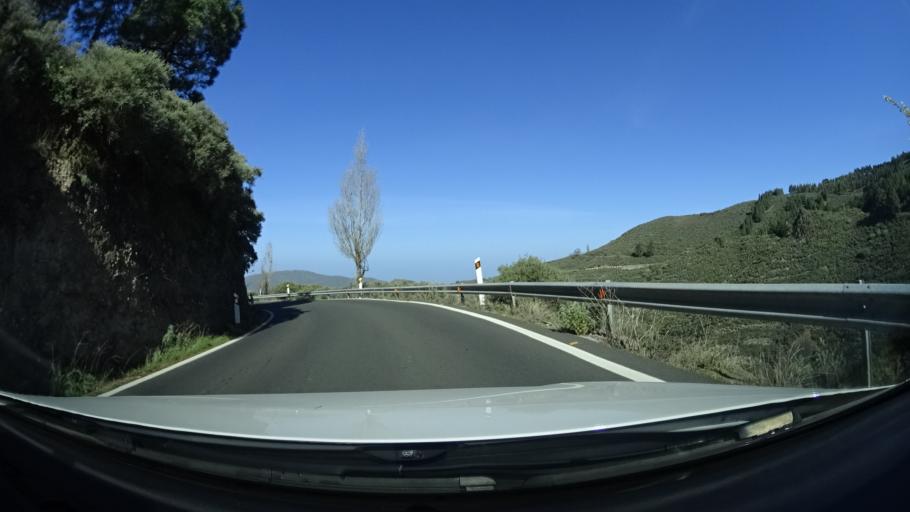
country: ES
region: Canary Islands
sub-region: Provincia de Las Palmas
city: Artenara
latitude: 28.0267
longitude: -15.6211
